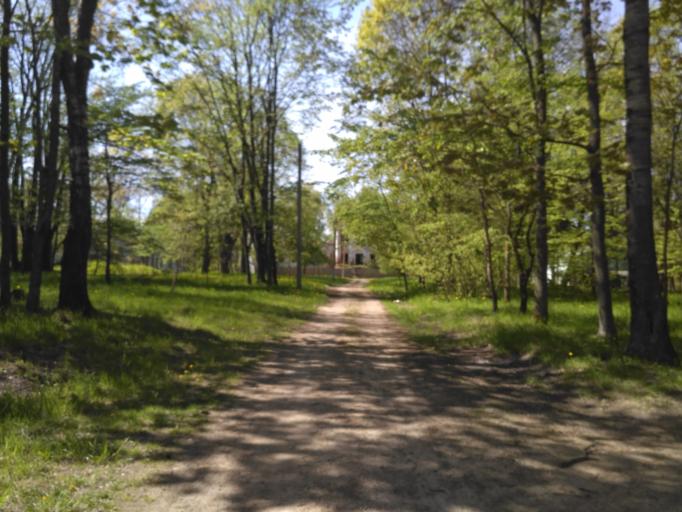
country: BY
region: Minsk
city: Chervyen'
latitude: 53.8837
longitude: 28.6172
